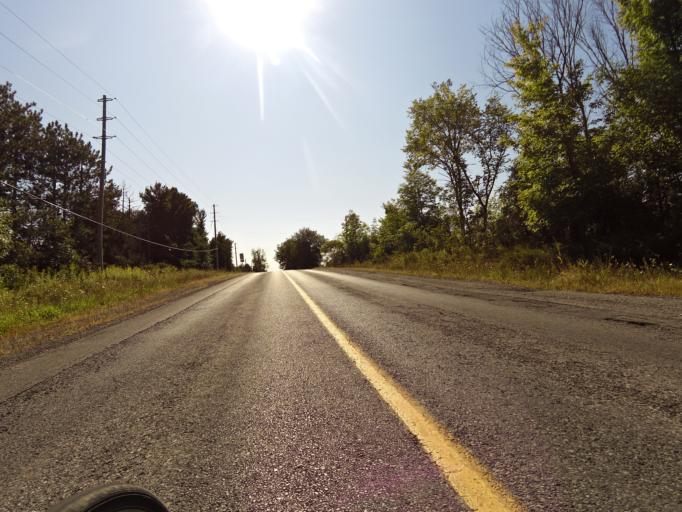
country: CA
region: Ontario
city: Bells Corners
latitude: 45.4545
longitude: -75.9685
